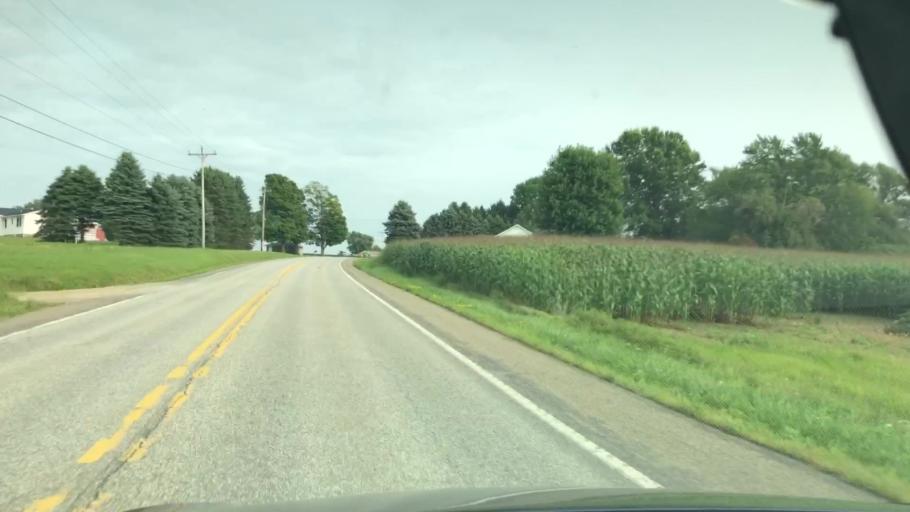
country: US
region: Pennsylvania
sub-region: Erie County
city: Union City
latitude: 41.8689
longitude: -79.8373
